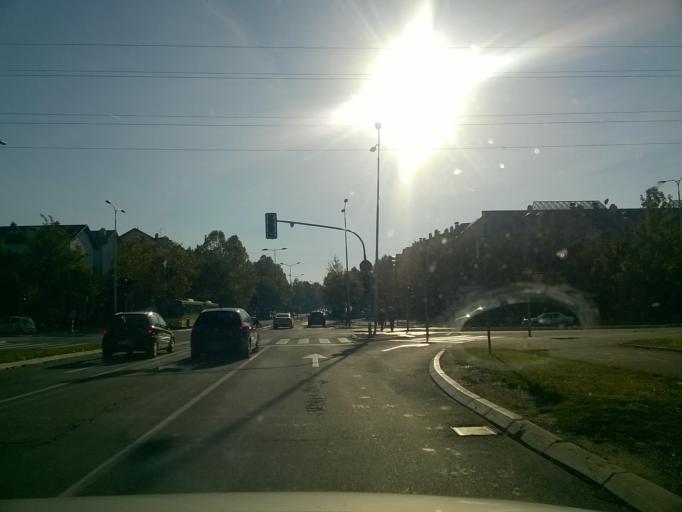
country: RS
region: Central Serbia
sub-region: Belgrade
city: Zemun
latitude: 44.8185
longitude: 20.3851
